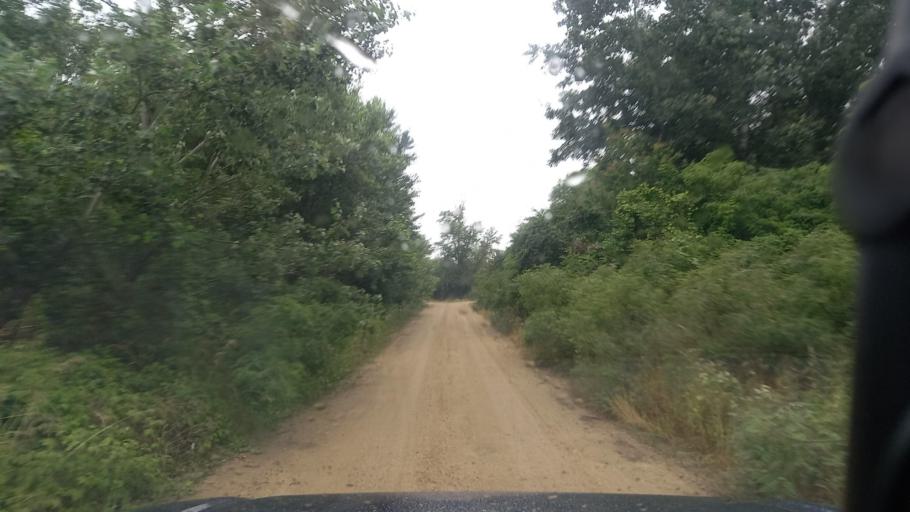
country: RU
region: Krasnodarskiy
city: Vasyurinskaya
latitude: 45.0325
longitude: 39.4742
